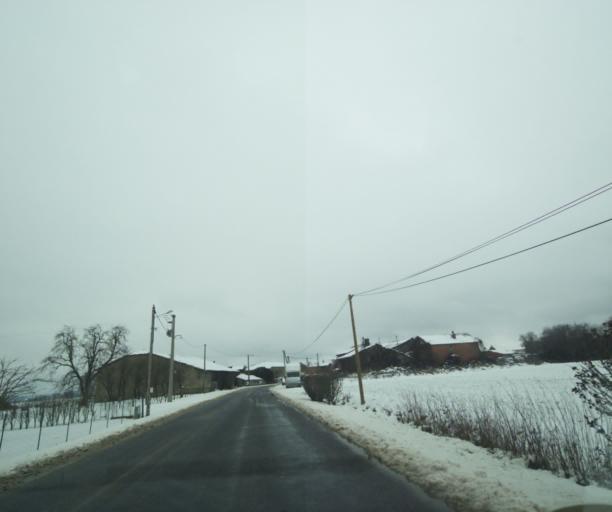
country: FR
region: Champagne-Ardenne
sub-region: Departement de la Haute-Marne
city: Montier-en-Der
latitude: 48.4426
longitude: 4.8030
